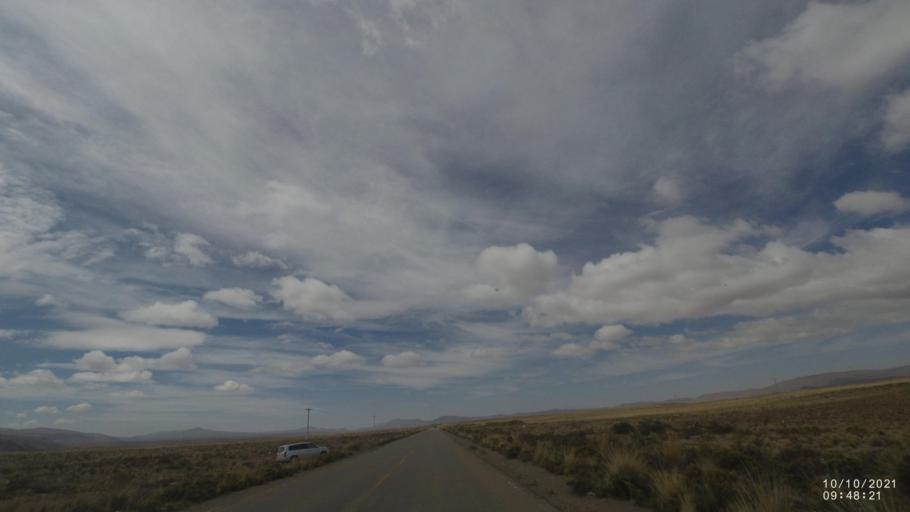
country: BO
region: La Paz
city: Quime
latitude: -17.2083
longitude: -67.3418
